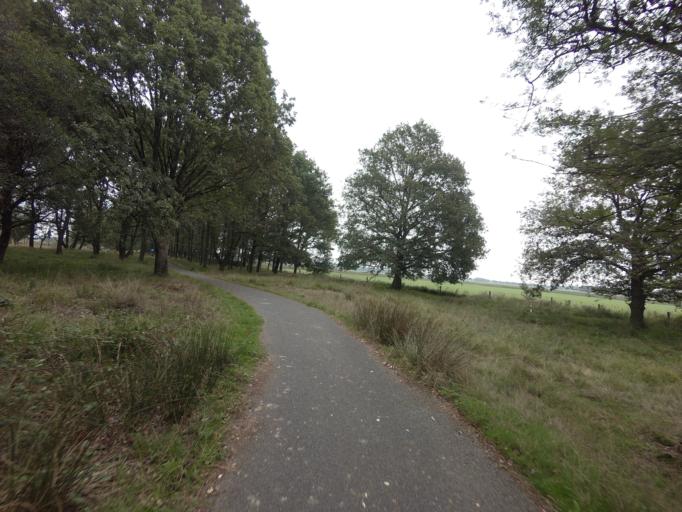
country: NL
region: Drenthe
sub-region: Gemeente Assen
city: Assen
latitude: 52.9083
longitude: 6.4847
